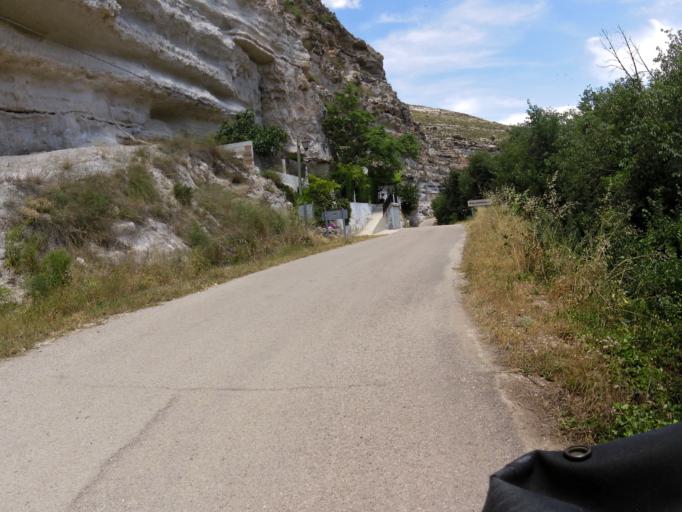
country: ES
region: Castille-La Mancha
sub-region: Provincia de Albacete
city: Jorquera
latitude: 39.1610
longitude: -1.5663
